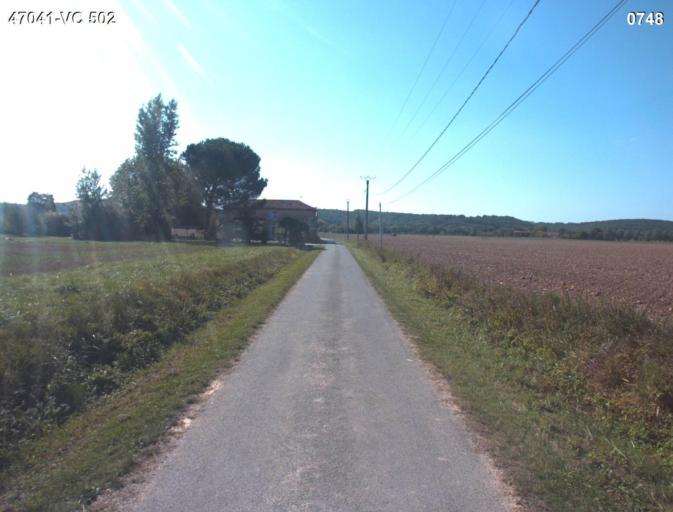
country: FR
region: Aquitaine
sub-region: Departement du Lot-et-Garonne
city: Port-Sainte-Marie
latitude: 44.2254
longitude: 0.3947
